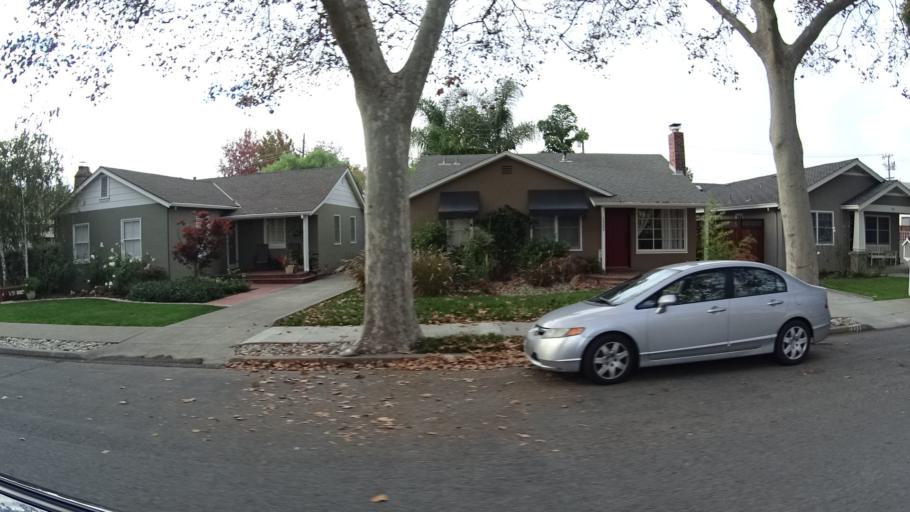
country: US
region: California
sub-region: Santa Clara County
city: Buena Vista
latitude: 37.3267
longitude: -121.9138
